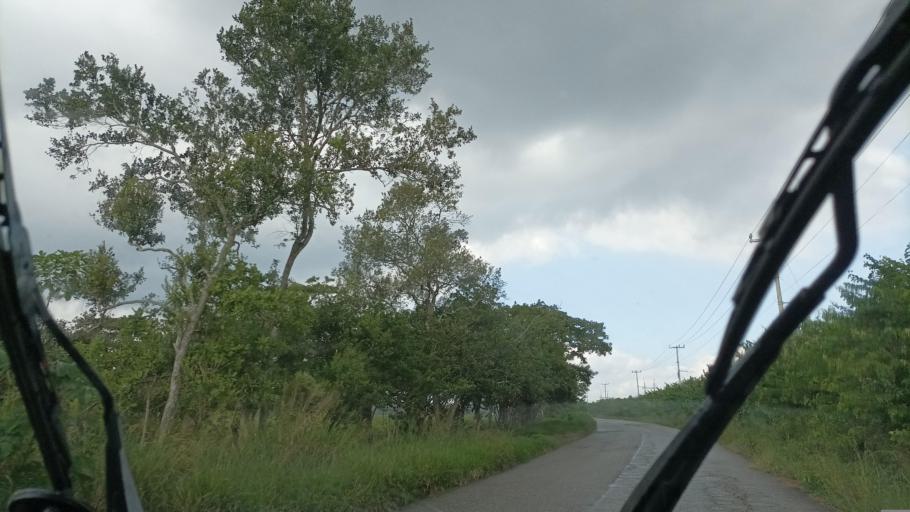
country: MX
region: Veracruz
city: Las Choapas
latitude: 17.8386
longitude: -94.1041
